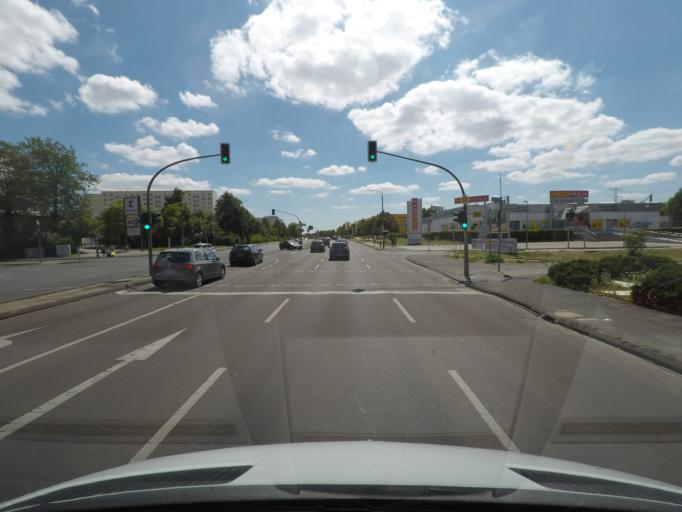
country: DE
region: Berlin
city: Biesdorf
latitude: 52.5348
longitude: 13.5370
